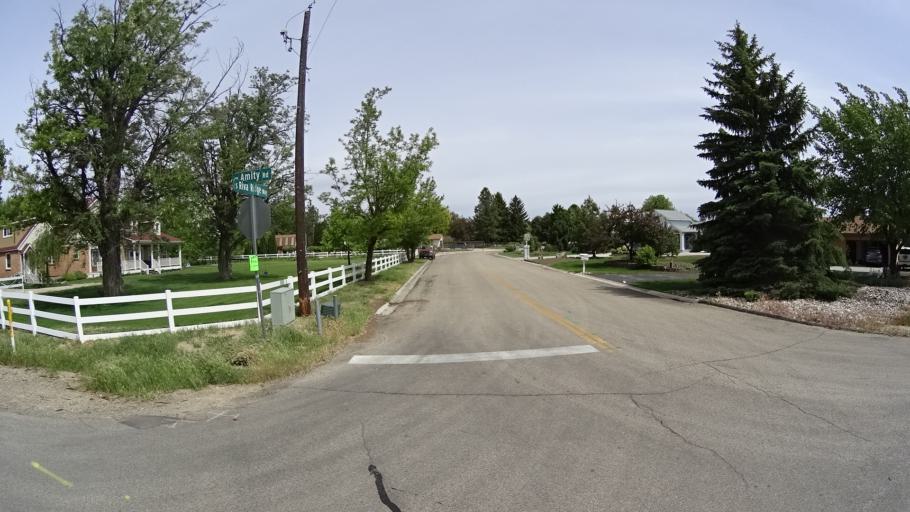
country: US
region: Idaho
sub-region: Ada County
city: Meridian
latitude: 43.5612
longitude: -116.3262
